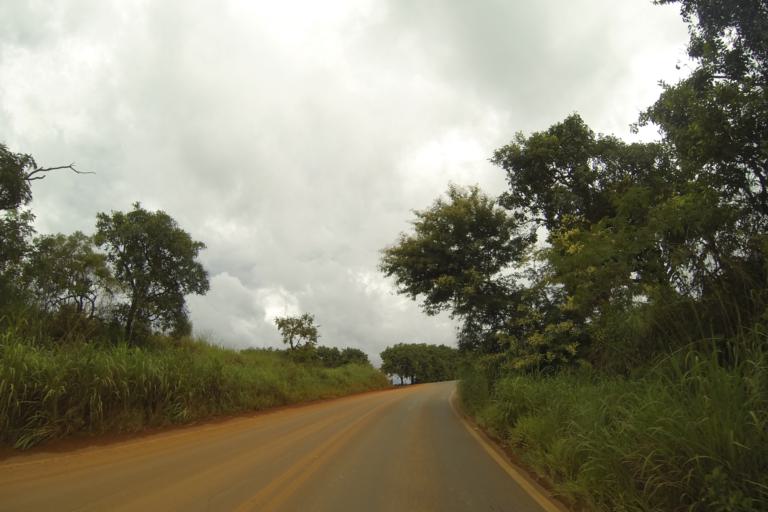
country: BR
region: Minas Gerais
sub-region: Bambui
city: Bambui
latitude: -20.0741
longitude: -46.1551
